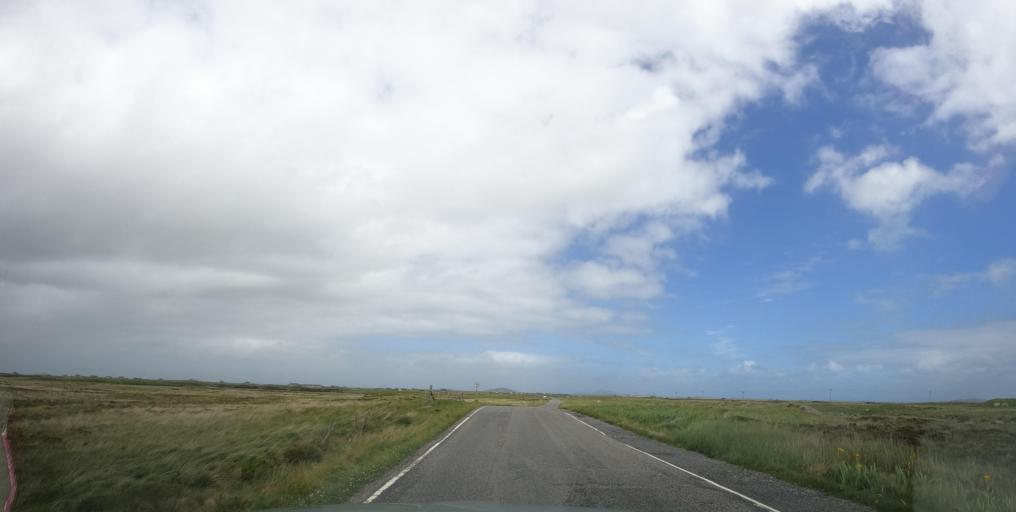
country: GB
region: Scotland
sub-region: Eilean Siar
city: Benbecula
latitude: 57.3806
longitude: -7.3424
